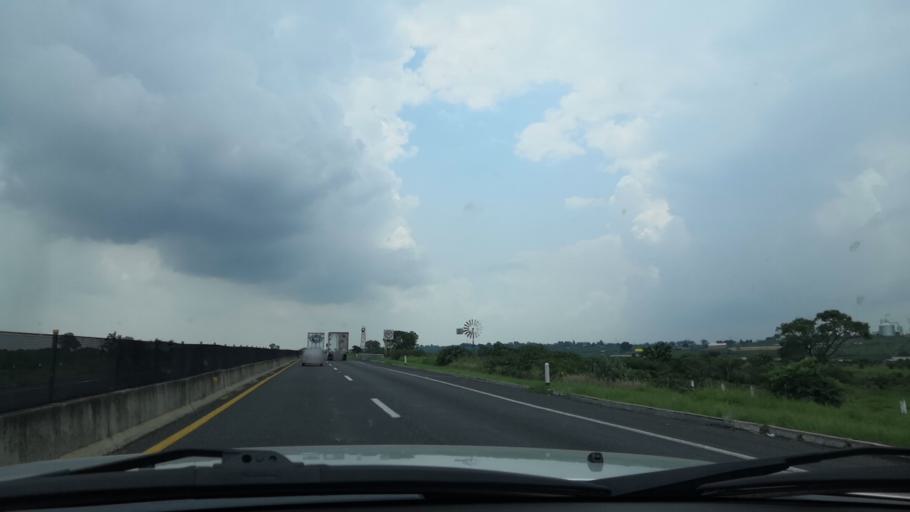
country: MX
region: Jalisco
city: Acatic
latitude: 20.7178
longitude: -102.9421
